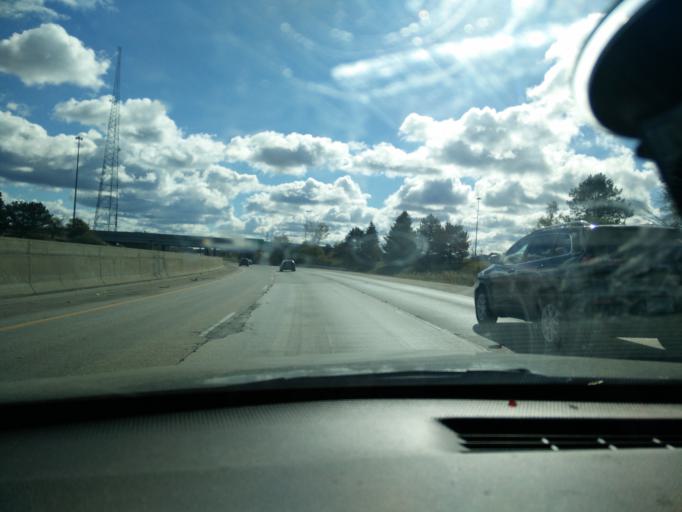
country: US
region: Michigan
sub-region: Oakland County
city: Bingham Farms
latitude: 42.4909
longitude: -83.2873
